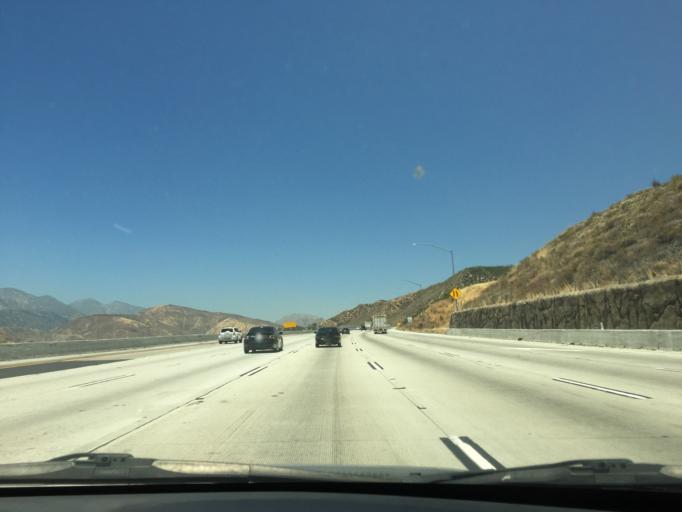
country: US
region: California
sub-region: San Bernardino County
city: Muscoy
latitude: 34.2414
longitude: -117.4312
